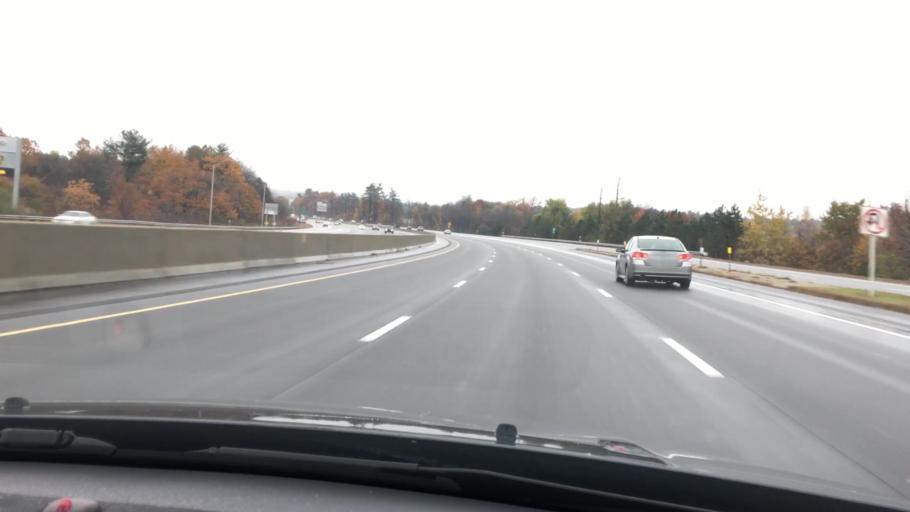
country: US
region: New Hampshire
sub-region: Hillsborough County
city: Nashua
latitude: 42.7437
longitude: -71.4910
